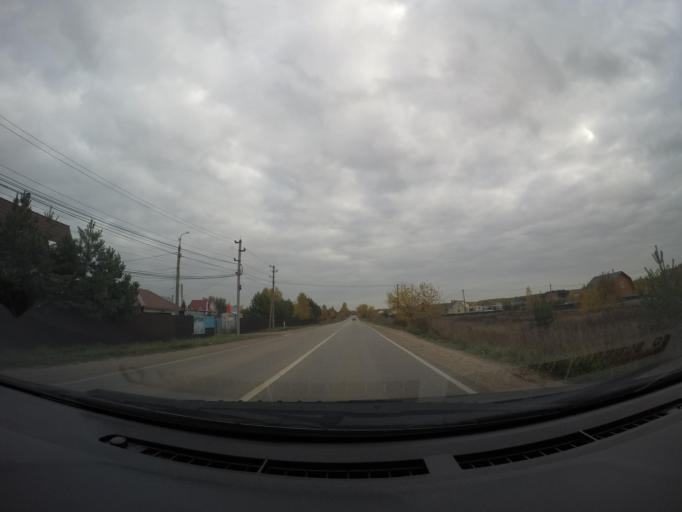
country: RU
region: Moskovskaya
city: Gzhel'
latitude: 55.6419
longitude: 38.3965
